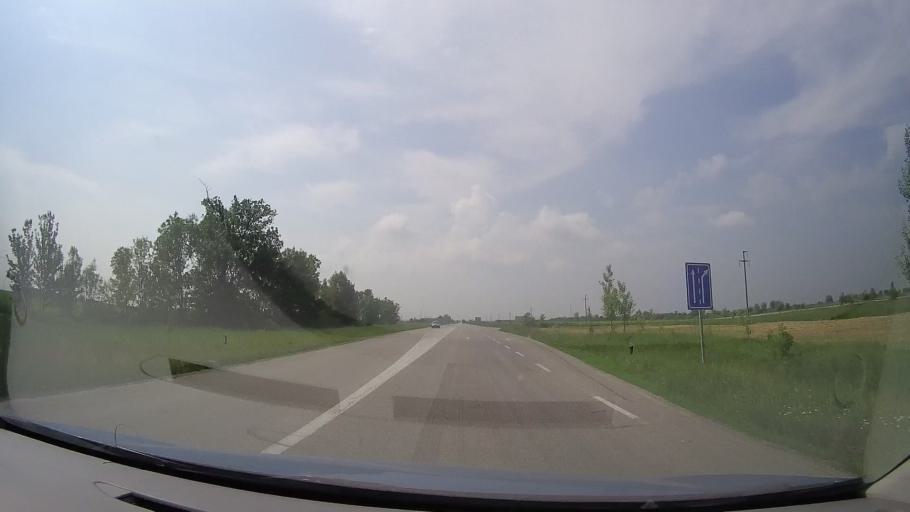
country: RS
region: Autonomna Pokrajina Vojvodina
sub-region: Juznobanatski Okrug
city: Kovacica
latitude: 45.0782
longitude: 20.6411
